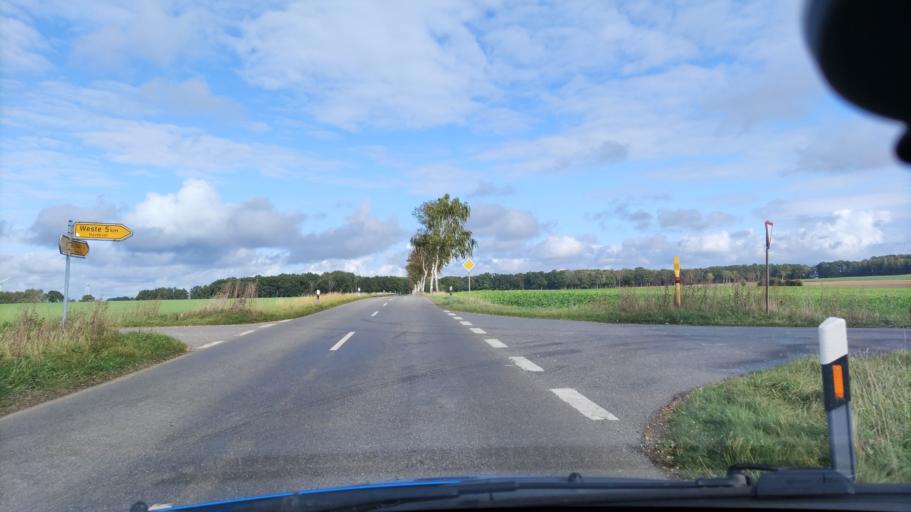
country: DE
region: Lower Saxony
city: Romstedt
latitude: 53.0860
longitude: 10.6726
